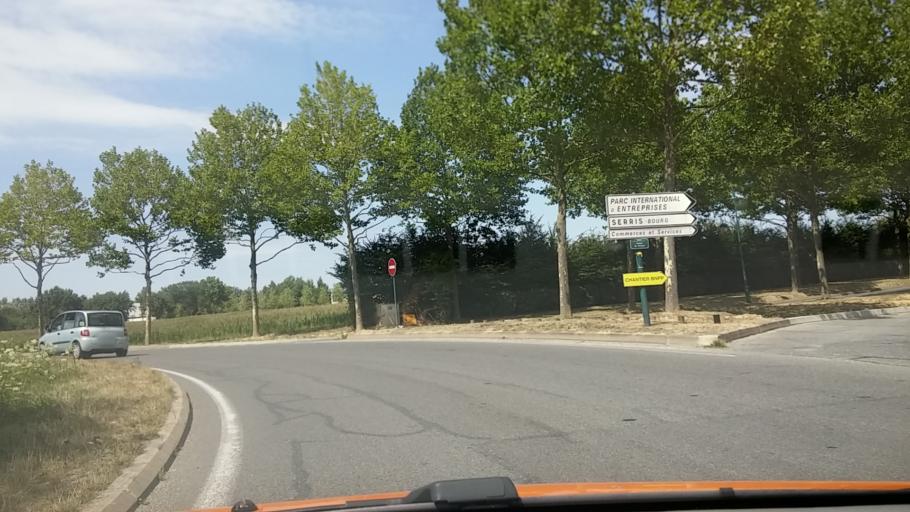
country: FR
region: Ile-de-France
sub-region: Departement de Seine-et-Marne
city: Serris
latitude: 48.8359
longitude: 2.7923
